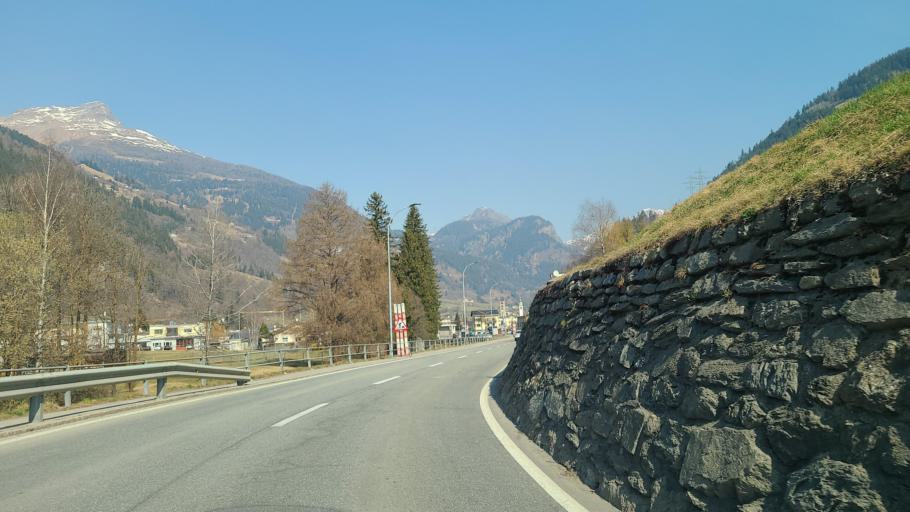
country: CH
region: Grisons
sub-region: Bernina District
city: Poschiavo
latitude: 46.3179
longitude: 10.0593
